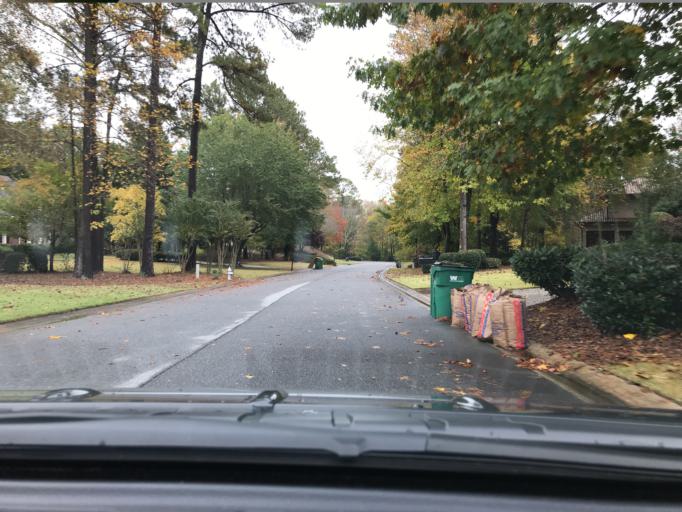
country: US
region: Georgia
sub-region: Fulton County
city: Johns Creek
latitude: 34.0089
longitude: -84.2304
